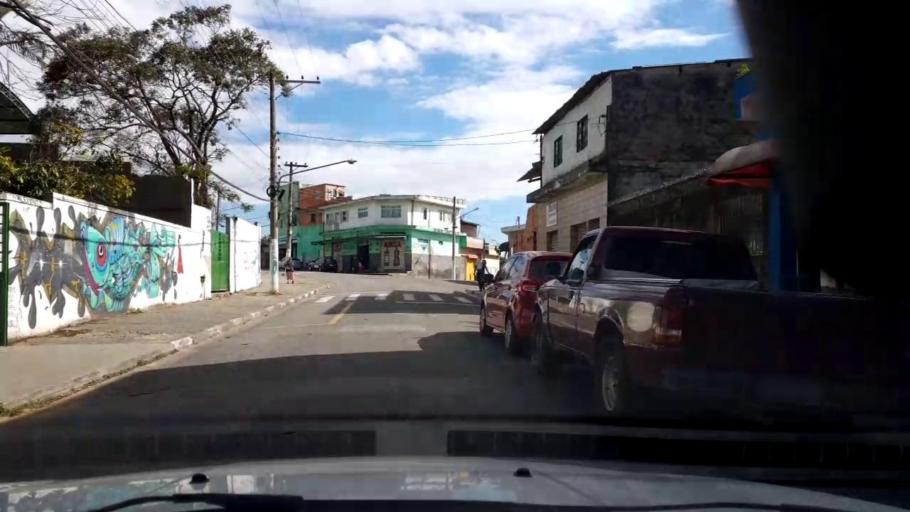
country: BR
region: Sao Paulo
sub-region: Ferraz De Vasconcelos
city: Ferraz de Vasconcelos
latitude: -23.5321
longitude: -46.3928
